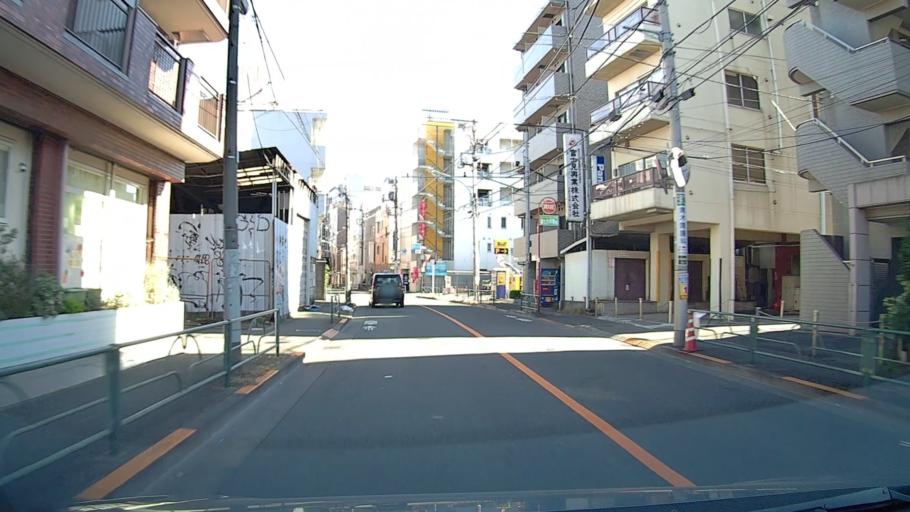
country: JP
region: Tokyo
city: Tokyo
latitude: 35.7003
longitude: 139.6604
